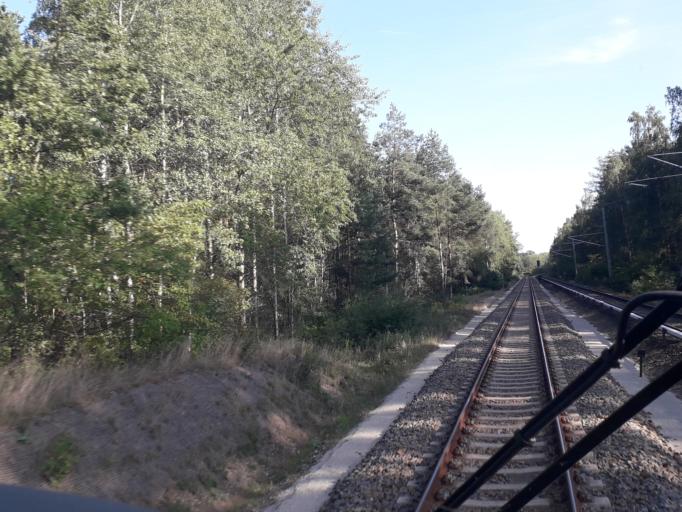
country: DE
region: Brandenburg
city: Velten
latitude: 52.6691
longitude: 13.1957
